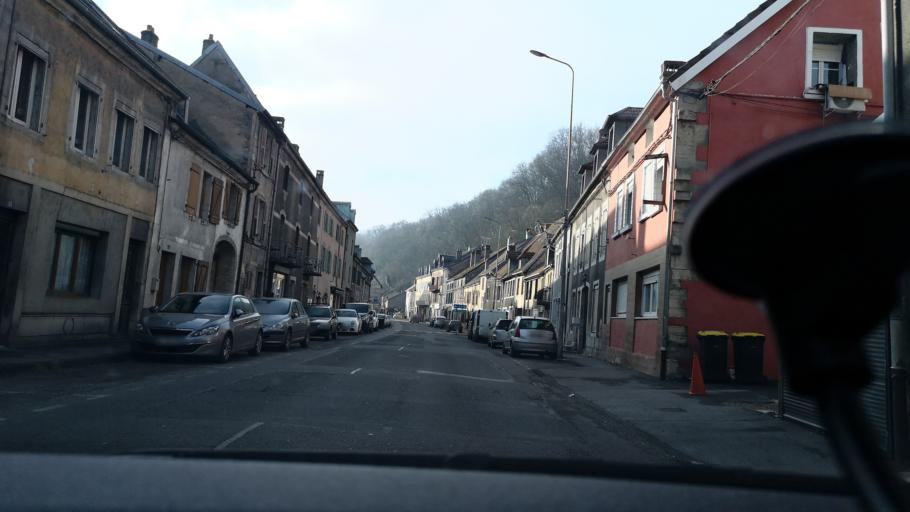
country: FR
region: Franche-Comte
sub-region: Departement du Doubs
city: Montenois
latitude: 47.4526
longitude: 6.5793
